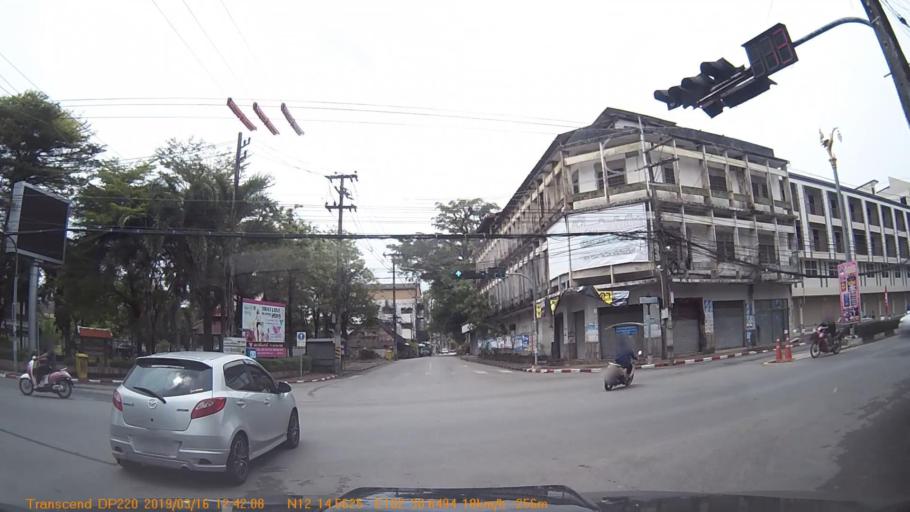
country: TH
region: Trat
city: Trat
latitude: 12.2427
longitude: 102.5107
